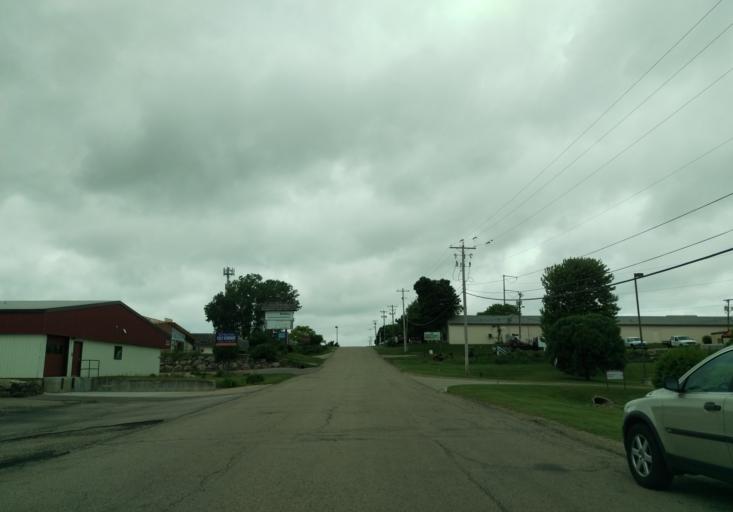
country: US
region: Wisconsin
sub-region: Dane County
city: Middleton
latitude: 43.0517
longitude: -89.4984
